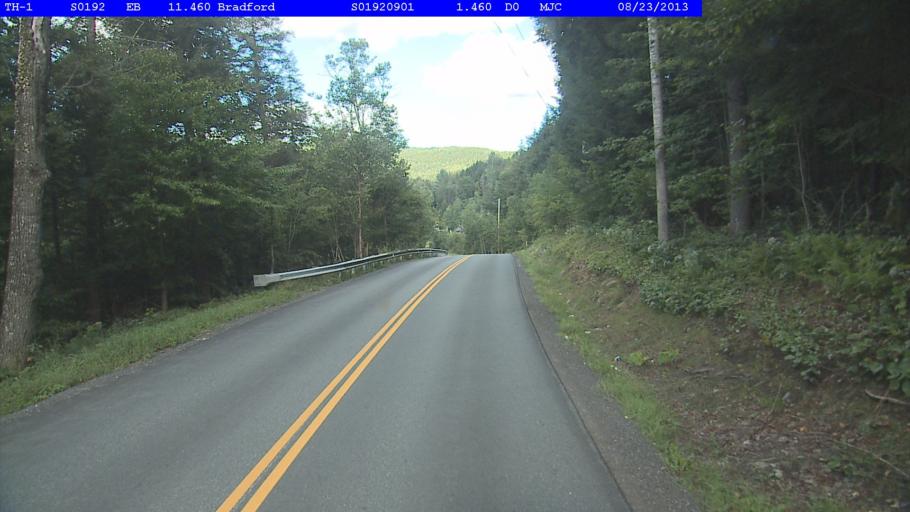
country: US
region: New Hampshire
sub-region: Grafton County
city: Haverhill
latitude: 44.0279
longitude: -72.1969
